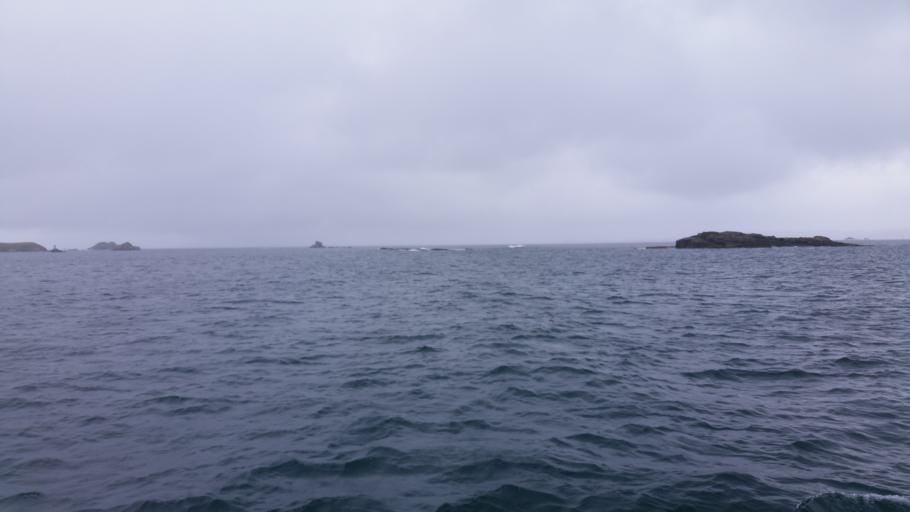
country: FR
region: Brittany
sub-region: Departement du Finistere
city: Carantec
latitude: 48.6944
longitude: -3.9163
